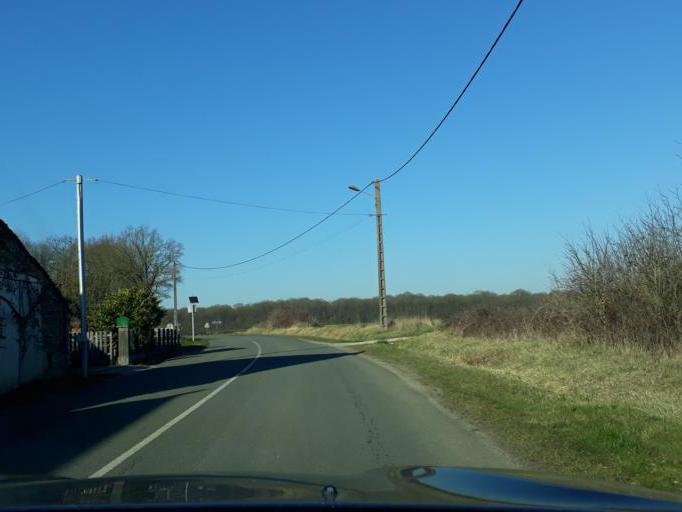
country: FR
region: Centre
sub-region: Departement du Loir-et-Cher
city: Oucques
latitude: 47.8398
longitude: 1.3814
